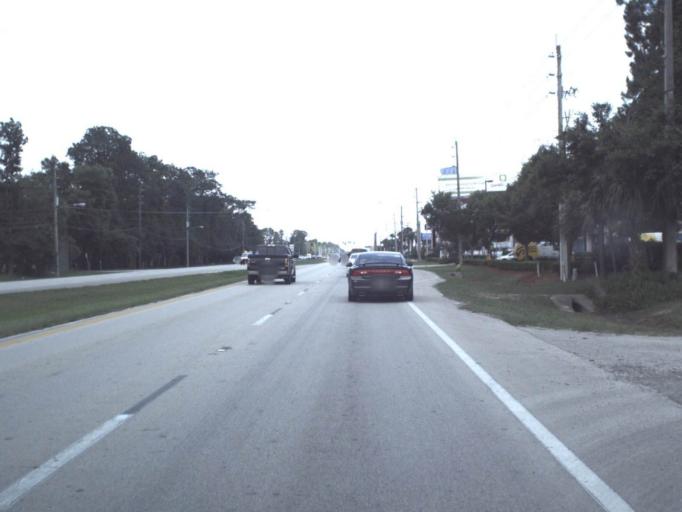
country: US
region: Florida
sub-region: Duval County
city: Jacksonville
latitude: 30.2300
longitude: -81.5911
